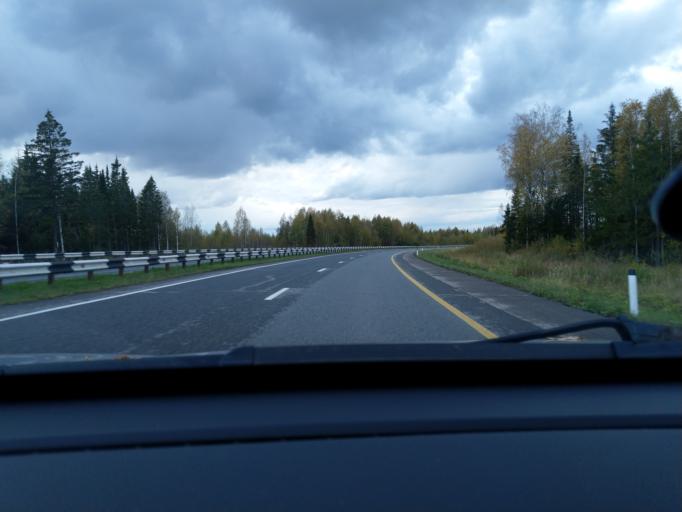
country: RU
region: Perm
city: Polazna
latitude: 58.3406
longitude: 56.4692
